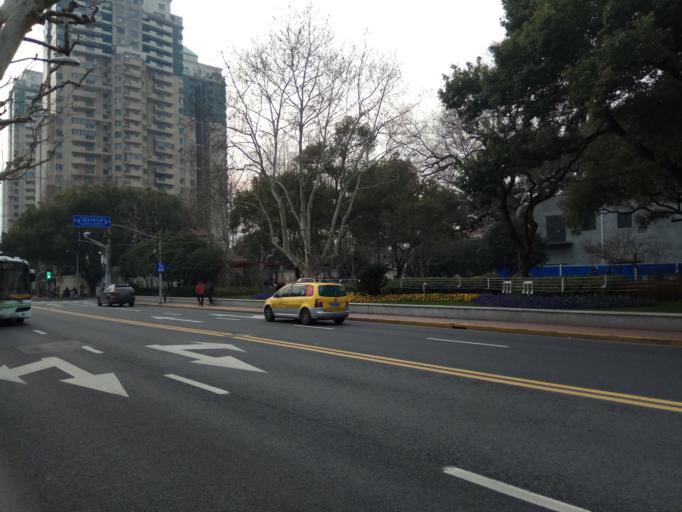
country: CN
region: Shanghai Shi
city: Xuhui
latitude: 31.2120
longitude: 121.4431
